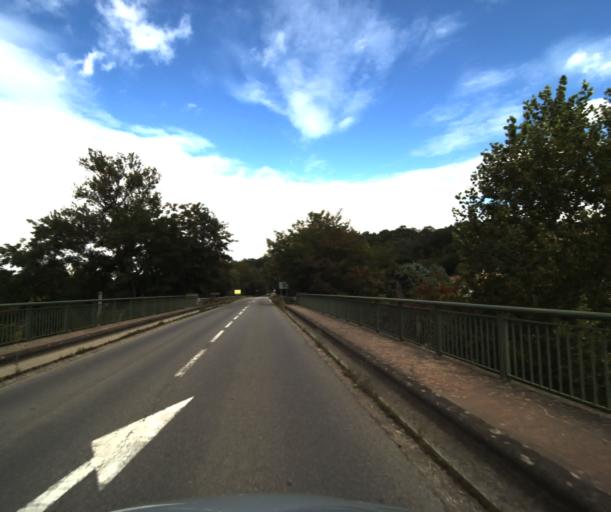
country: FR
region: Midi-Pyrenees
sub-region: Departement de la Haute-Garonne
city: Lacroix-Falgarde
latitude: 43.4992
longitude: 1.4076
